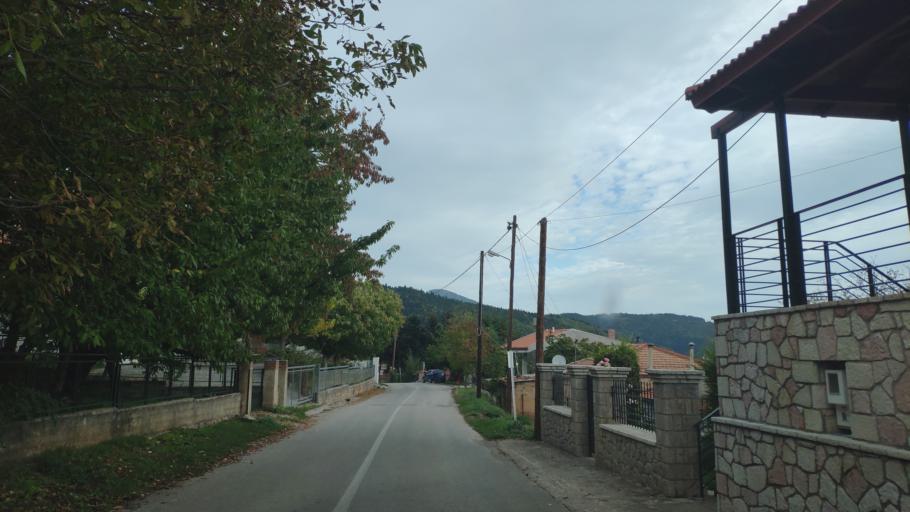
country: GR
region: Central Greece
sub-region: Nomos Fthiotidos
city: Stavros
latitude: 38.7342
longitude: 22.3461
